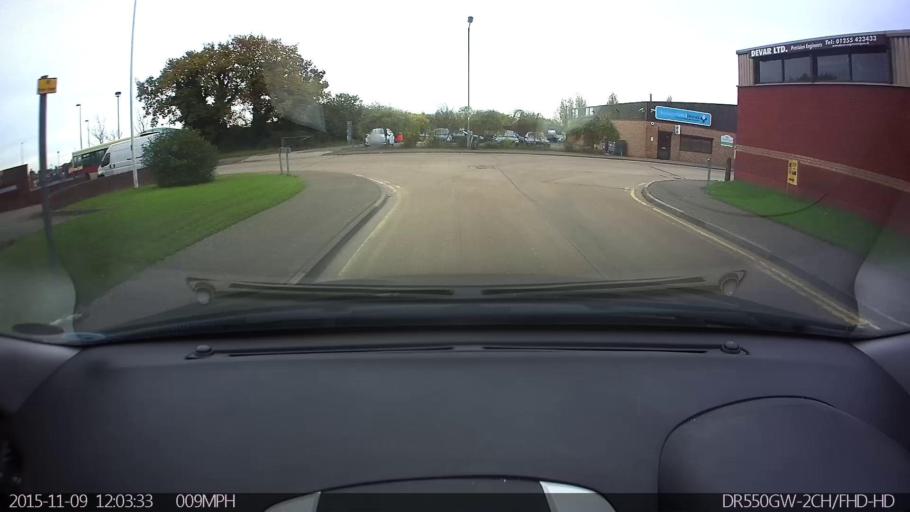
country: GB
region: England
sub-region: Essex
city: Little Clacton
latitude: 51.8186
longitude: 1.1656
